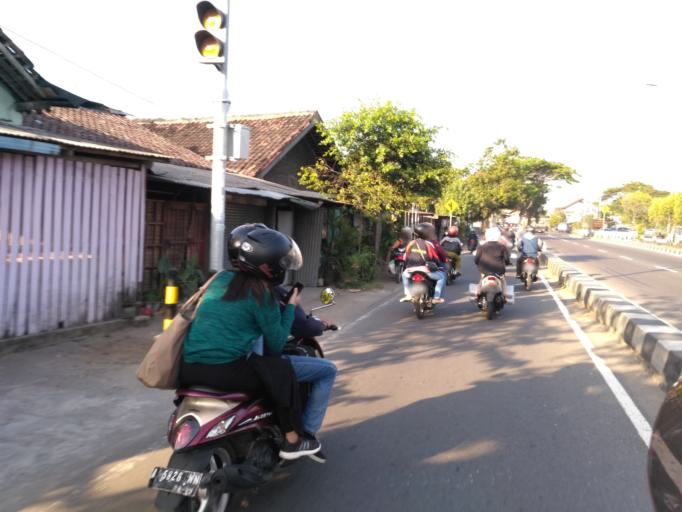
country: ID
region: Daerah Istimewa Yogyakarta
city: Sewon
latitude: -7.8339
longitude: 110.3869
